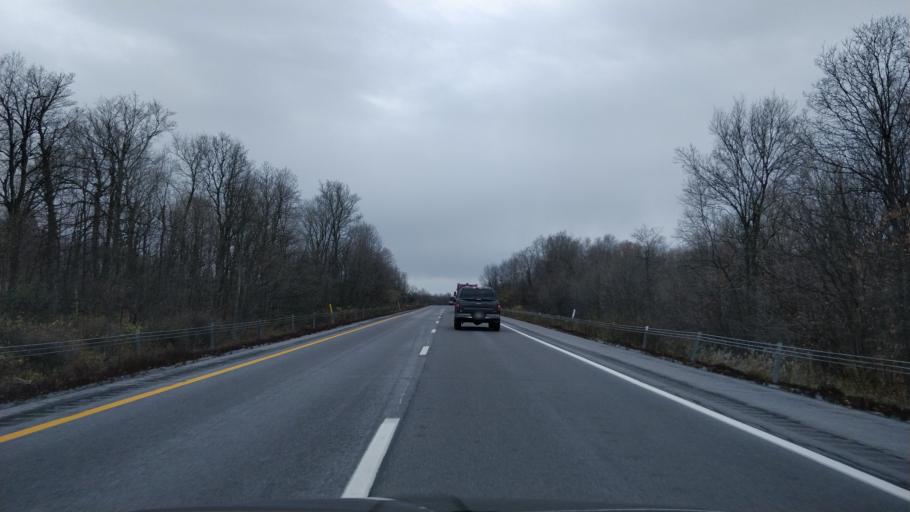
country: US
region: New York
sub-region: Jefferson County
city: Calcium
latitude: 44.1100
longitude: -75.8971
